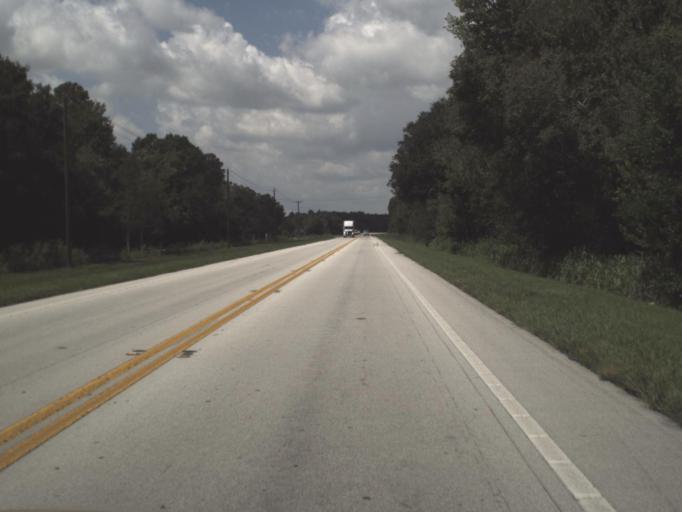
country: US
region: Florida
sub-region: Hillsborough County
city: Thonotosassa
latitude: 28.0849
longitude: -82.2730
